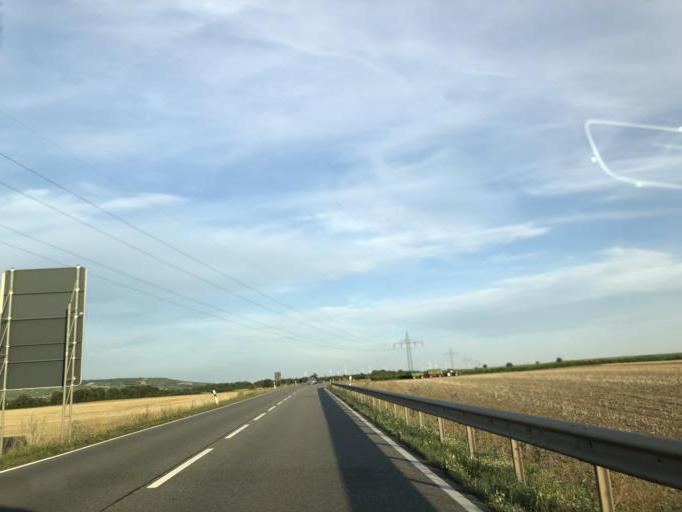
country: DE
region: Rheinland-Pfalz
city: Welgesheim
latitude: 49.8773
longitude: 7.9495
